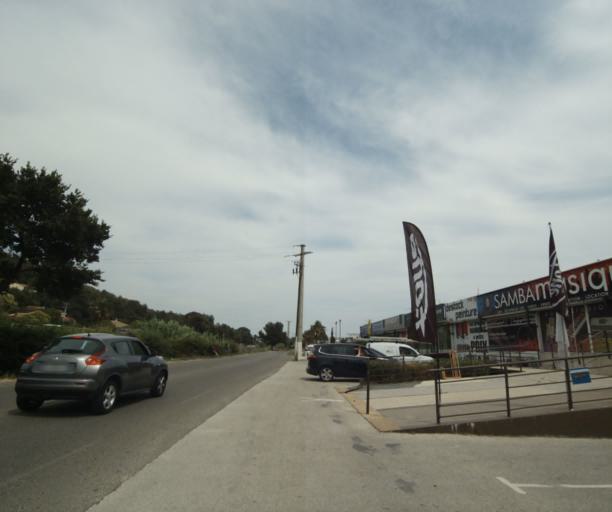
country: FR
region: Provence-Alpes-Cote d'Azur
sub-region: Departement du Var
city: La Garde
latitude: 43.1433
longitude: 6.0179
